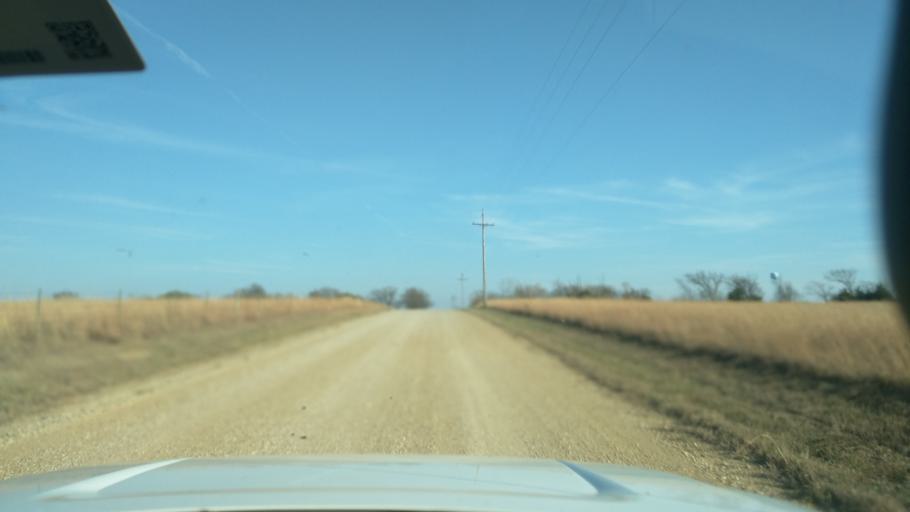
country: US
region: Kansas
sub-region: Lyon County
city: Emporia
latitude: 38.2890
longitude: -96.1776
